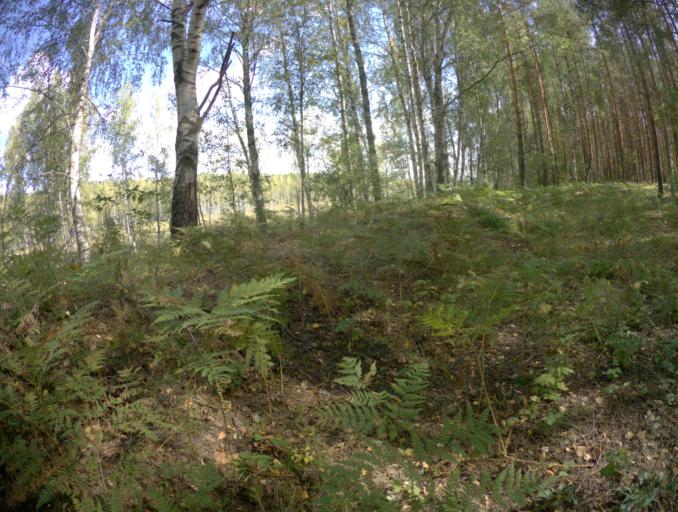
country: RU
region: Vladimir
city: Pokrov
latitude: 55.8479
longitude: 39.2207
